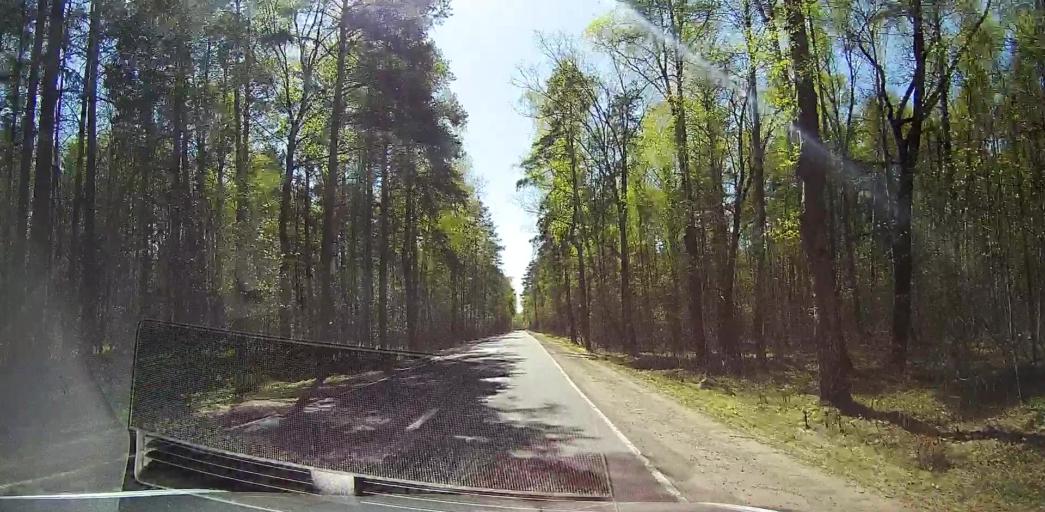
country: RU
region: Moskovskaya
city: Beloozerskiy
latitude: 55.4836
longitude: 38.4252
